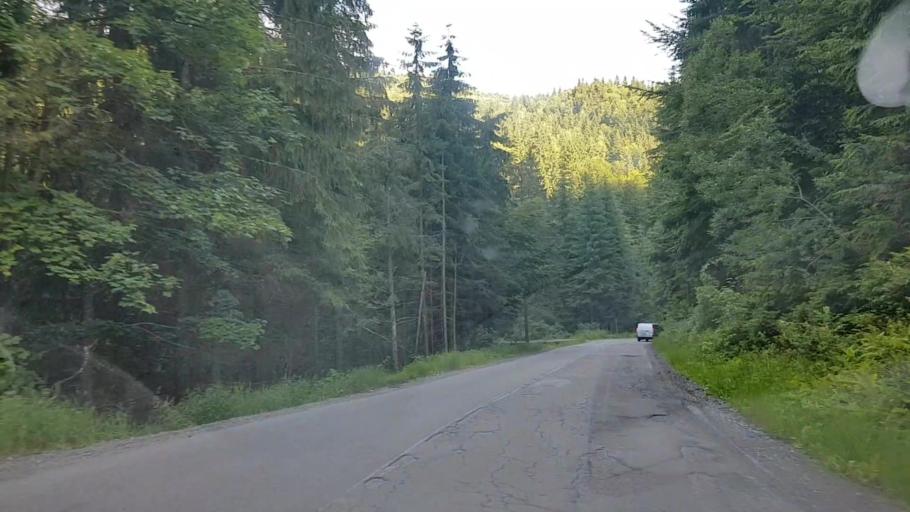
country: RO
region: Harghita
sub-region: Comuna Varsag
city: Varsag
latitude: 46.6345
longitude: 25.2650
